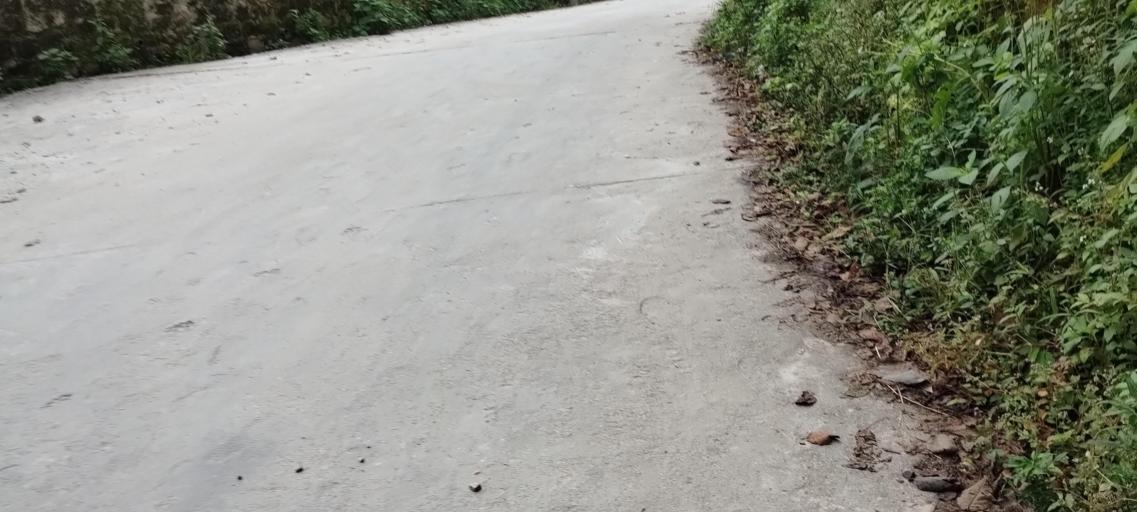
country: NP
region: Central Region
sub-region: Bagmati Zone
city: Kathmandu
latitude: 27.7834
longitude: 85.3623
